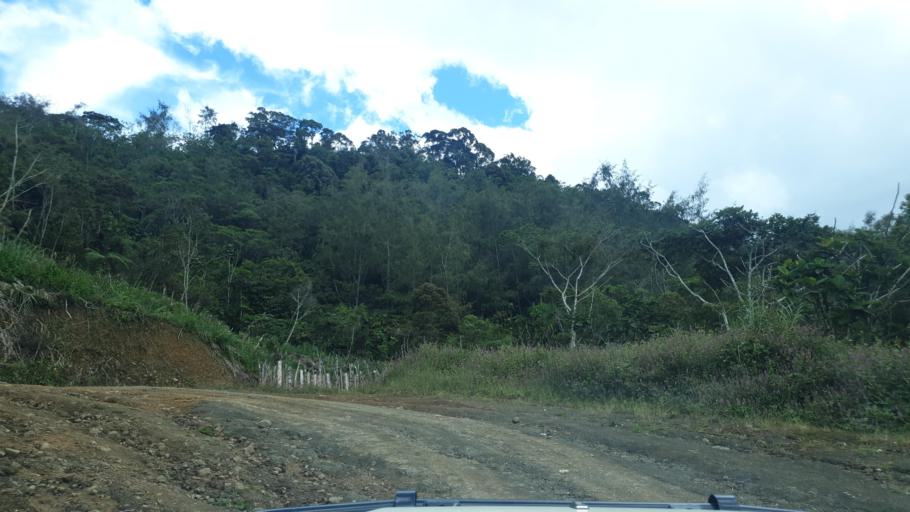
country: PG
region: Eastern Highlands
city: Goroka
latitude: -6.2786
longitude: 145.1889
